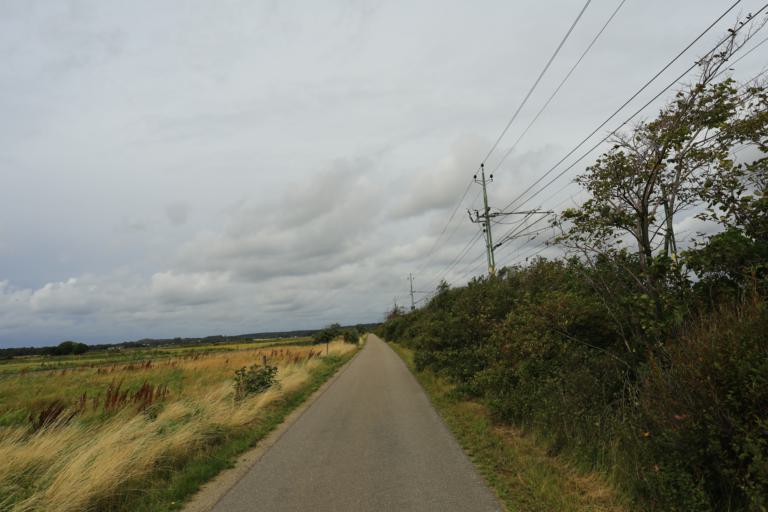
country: SE
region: Halland
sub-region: Varbergs Kommun
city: Varberg
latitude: 57.1319
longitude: 12.2603
